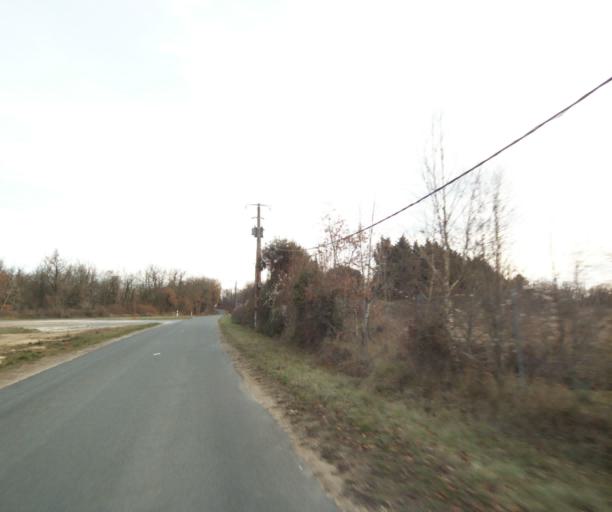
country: FR
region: Poitou-Charentes
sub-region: Departement de la Charente-Maritime
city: Fontcouverte
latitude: 45.8060
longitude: -0.5806
